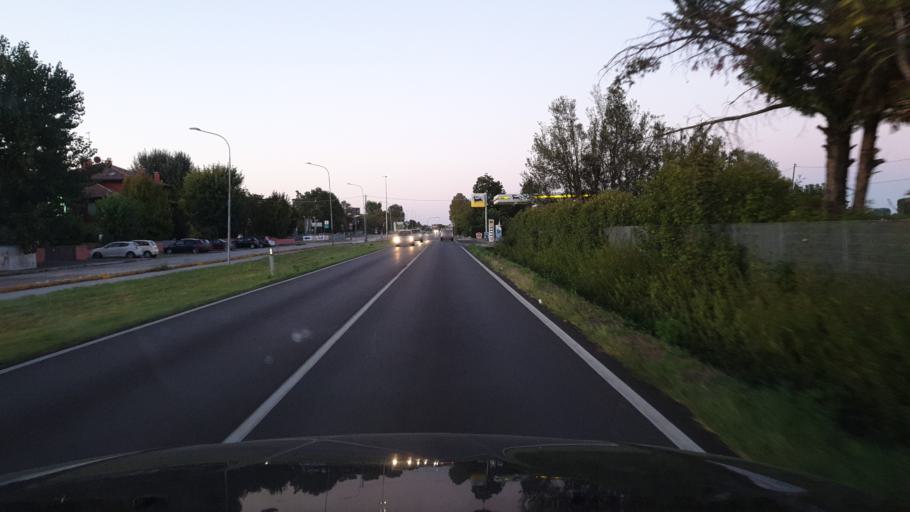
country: IT
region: Emilia-Romagna
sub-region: Provincia di Bologna
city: Altedo
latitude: 44.6776
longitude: 11.4938
